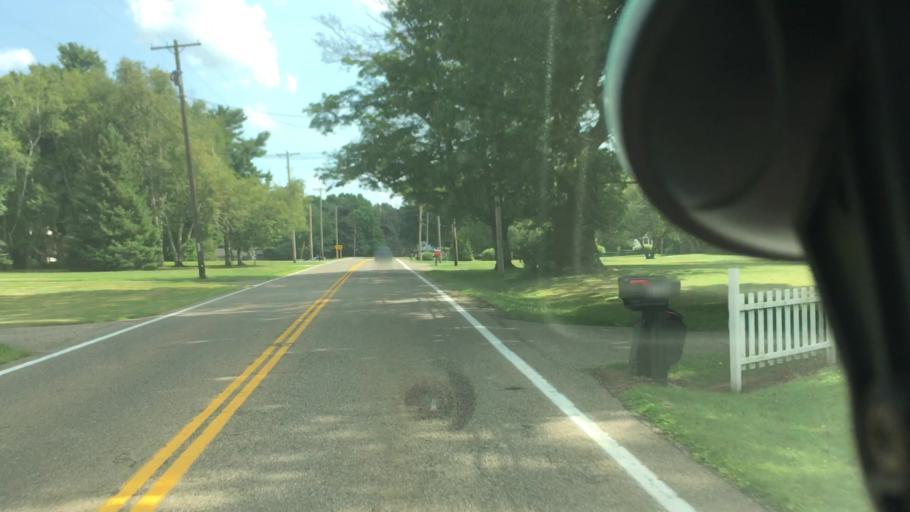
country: US
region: Ohio
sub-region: Columbiana County
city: Salem
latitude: 40.9203
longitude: -80.8404
